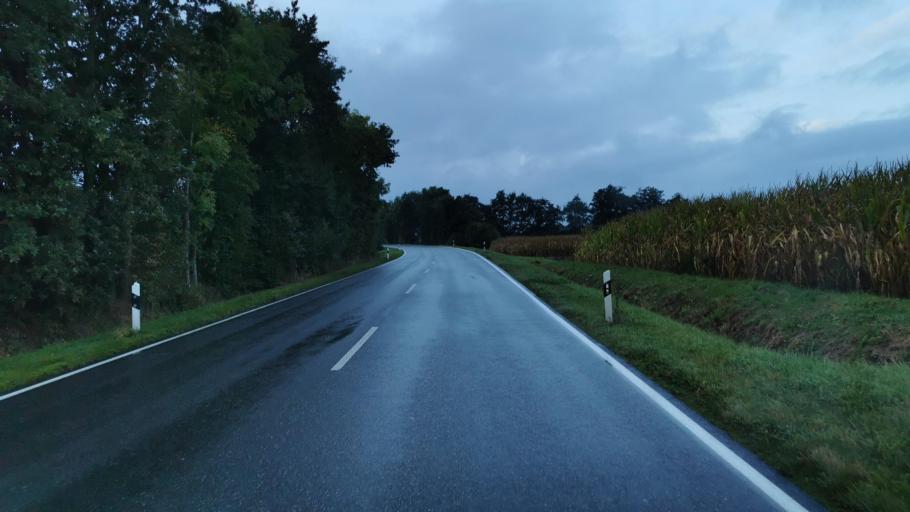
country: DE
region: North Rhine-Westphalia
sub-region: Regierungsbezirk Munster
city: Vreden
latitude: 52.1112
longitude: 6.8985
